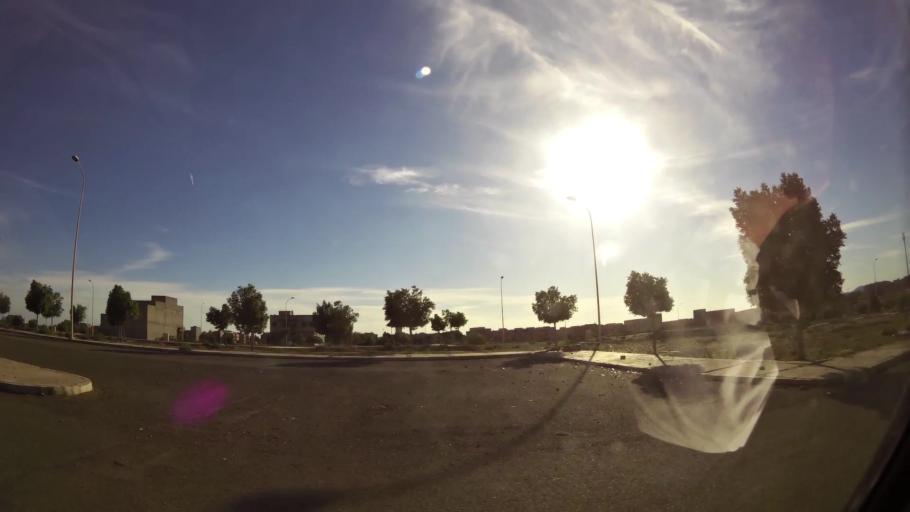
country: MA
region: Marrakech-Tensift-Al Haouz
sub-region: Marrakech
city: Marrakesh
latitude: 31.7599
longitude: -8.0944
